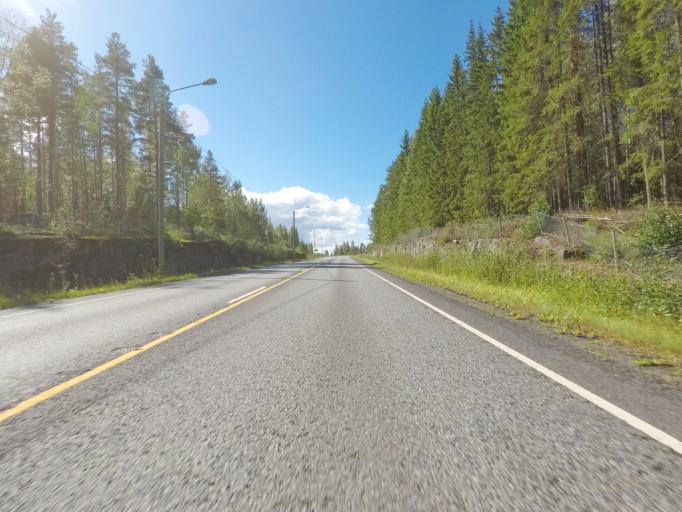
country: FI
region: Central Finland
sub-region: Jyvaeskylae
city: Hankasalmi
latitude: 62.3322
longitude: 26.5300
